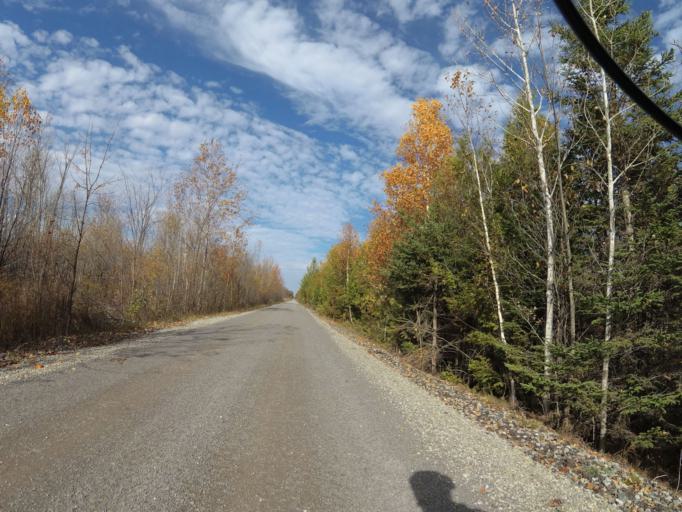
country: CA
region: Ontario
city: Carleton Place
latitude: 45.0548
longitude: -76.0912
